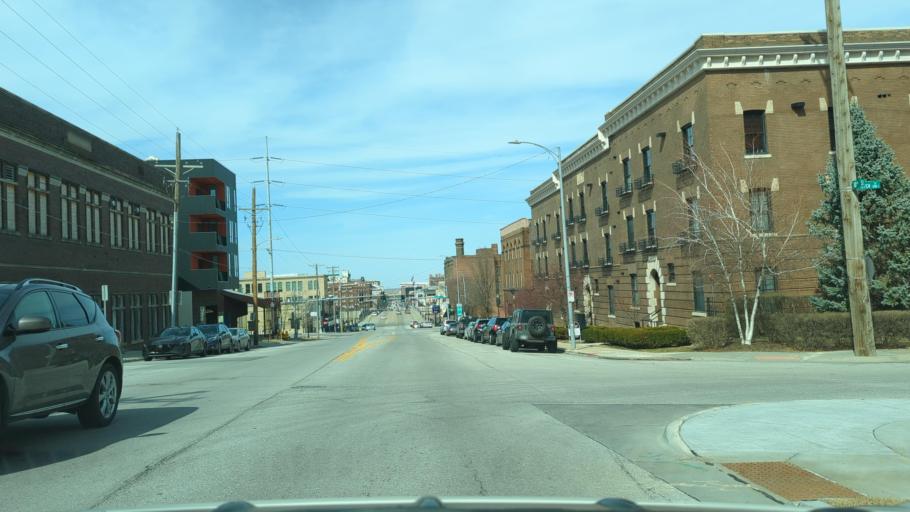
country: US
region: Nebraska
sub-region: Douglas County
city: Omaha
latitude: 41.2478
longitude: -95.9293
